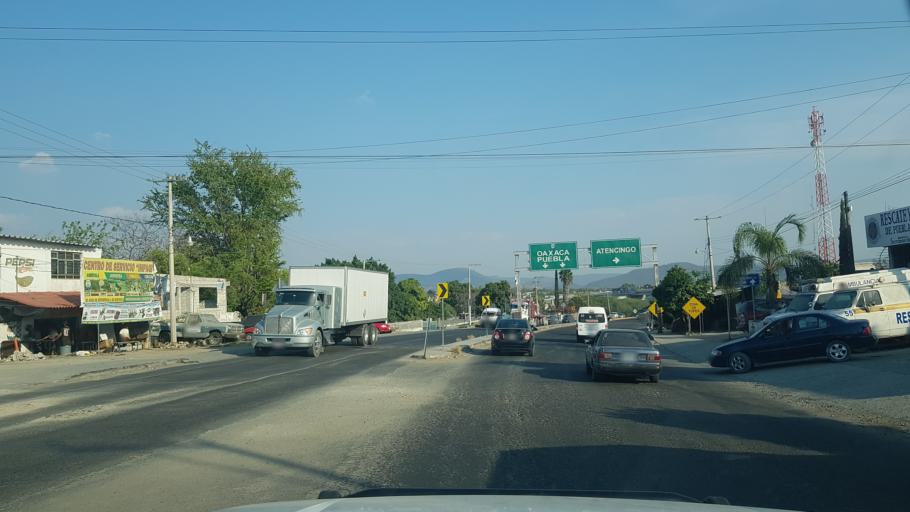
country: MX
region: Puebla
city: Izucar de Matamoros
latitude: 18.6027
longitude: -98.4822
